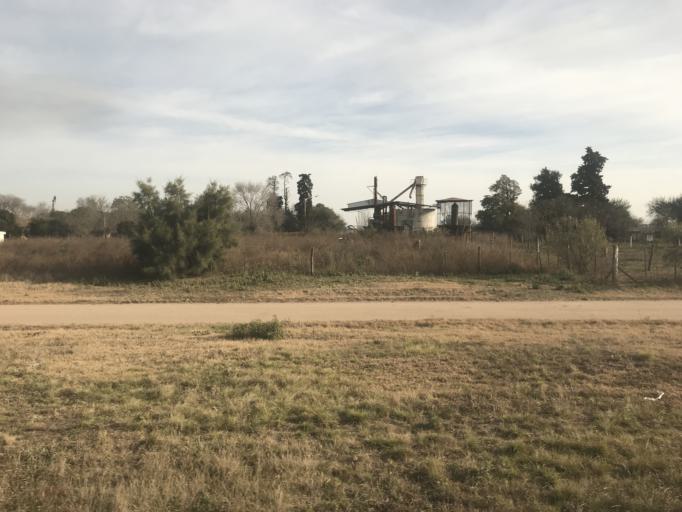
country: AR
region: Cordoba
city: Pilar
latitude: -31.6763
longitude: -63.8909
